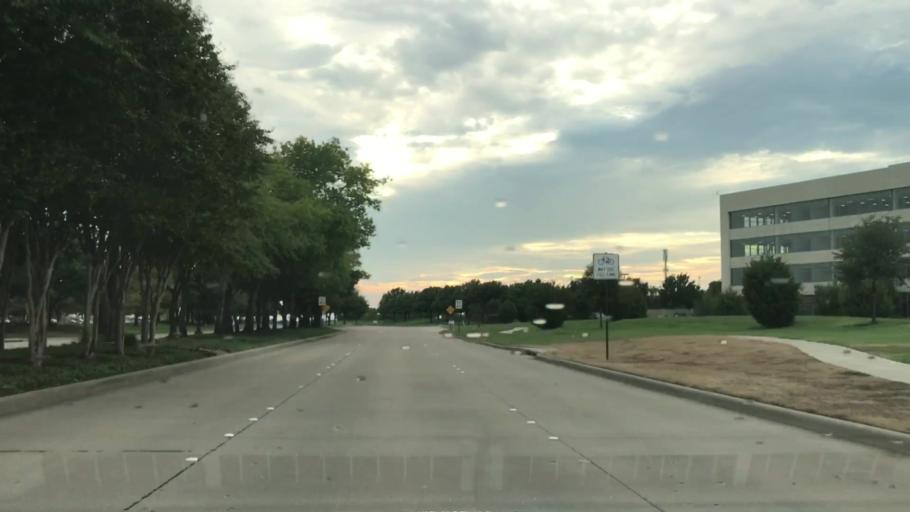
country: US
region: Texas
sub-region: Denton County
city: The Colony
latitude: 33.0722
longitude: -96.8288
